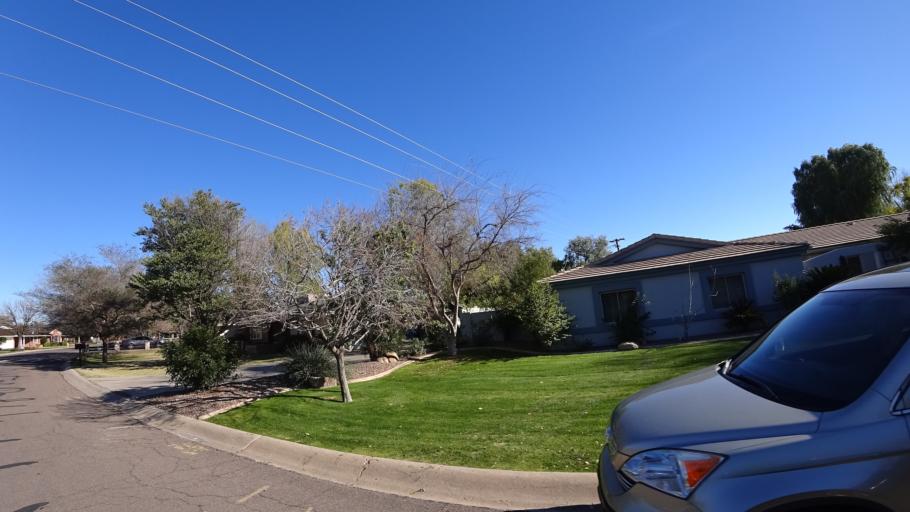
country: US
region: Arizona
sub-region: Maricopa County
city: Phoenix
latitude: 33.5431
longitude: -112.0776
